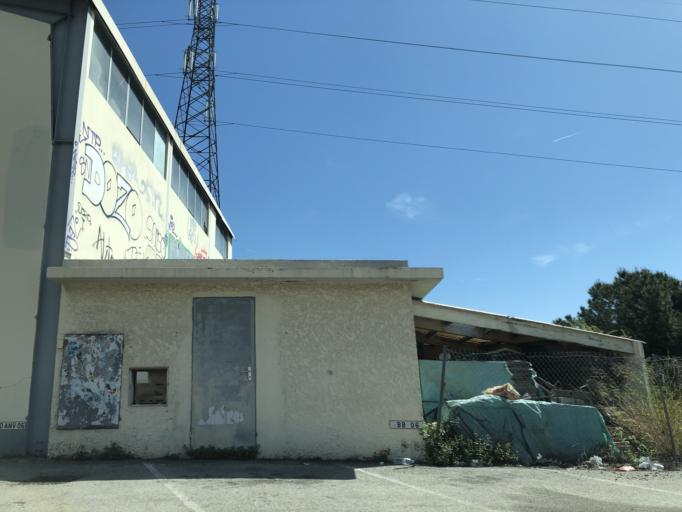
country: FR
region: Provence-Alpes-Cote d'Azur
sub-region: Departement des Alpes-Maritimes
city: Saint-Laurent-du-Var
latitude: 43.6991
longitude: 7.1841
